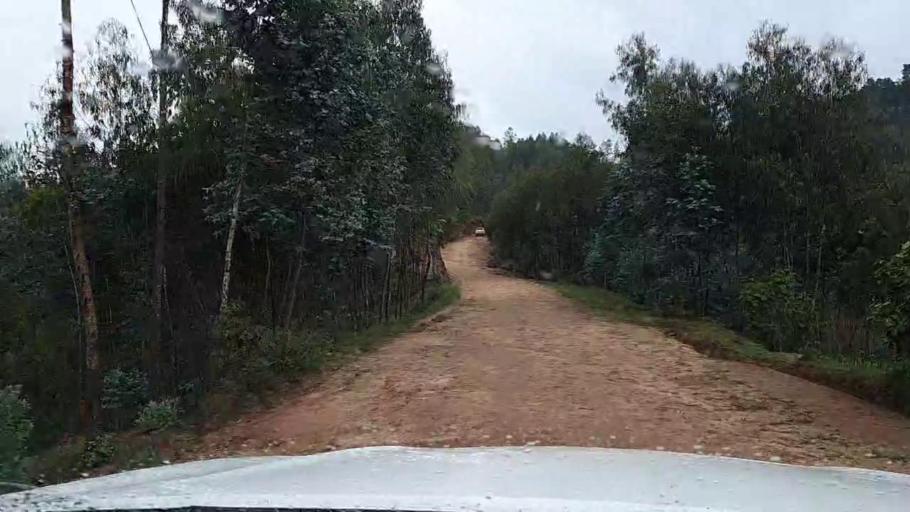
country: RW
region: Southern Province
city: Nzega
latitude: -2.4605
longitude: 29.4935
